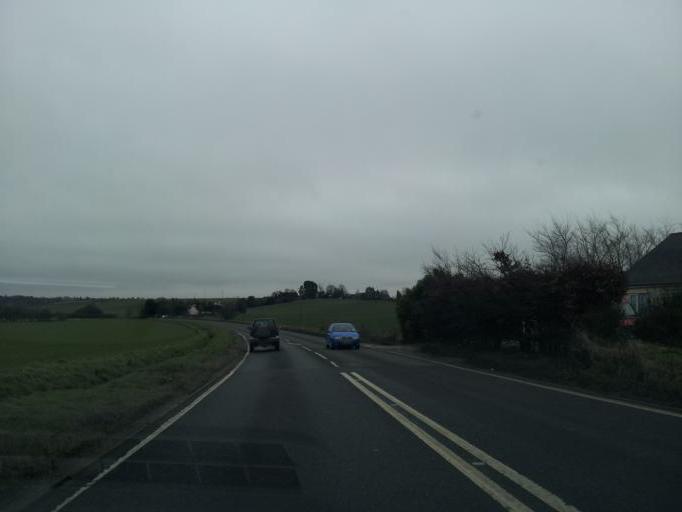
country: GB
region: England
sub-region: Suffolk
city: Shotley Gate
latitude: 51.9237
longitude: 1.1906
